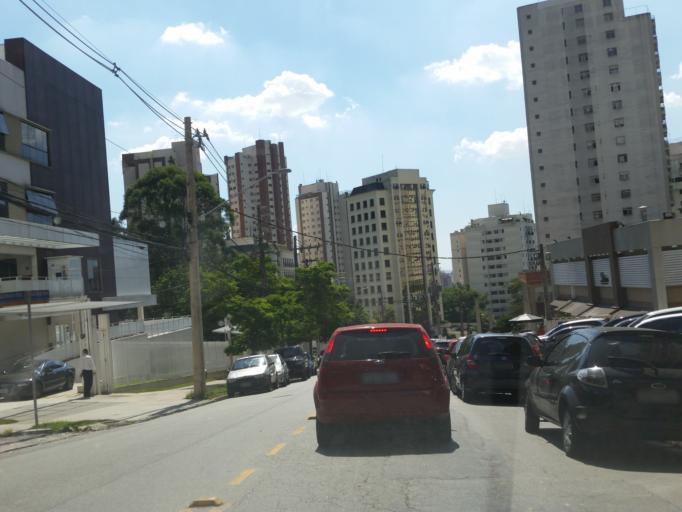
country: BR
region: Sao Paulo
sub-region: Taboao Da Serra
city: Taboao da Serra
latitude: -23.6195
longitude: -46.7405
